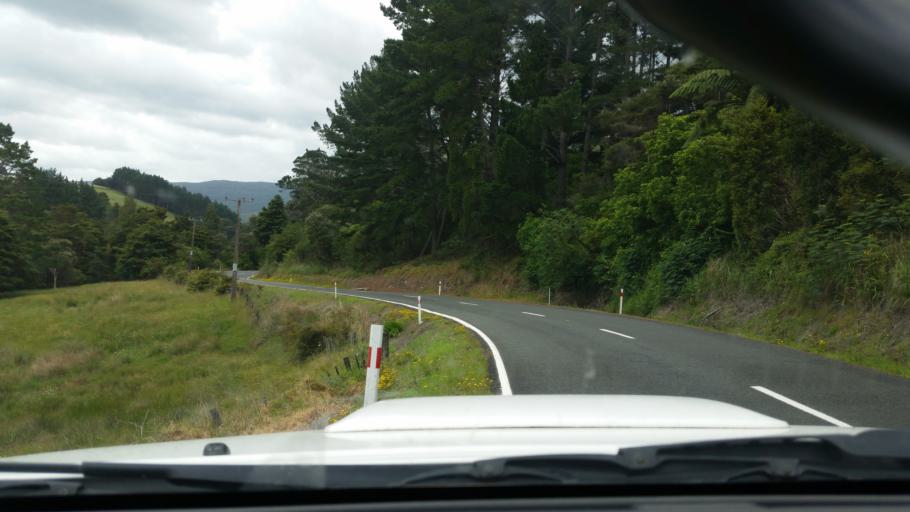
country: NZ
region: Northland
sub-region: Kaipara District
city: Dargaville
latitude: -35.8150
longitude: 173.7267
